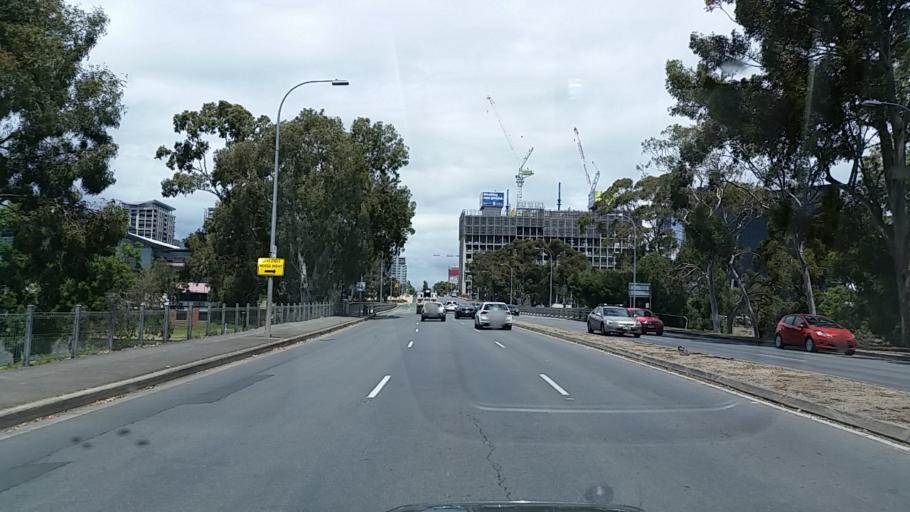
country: AU
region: South Australia
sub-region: Adelaide
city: North Adelaide
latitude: -34.9182
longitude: 138.5931
